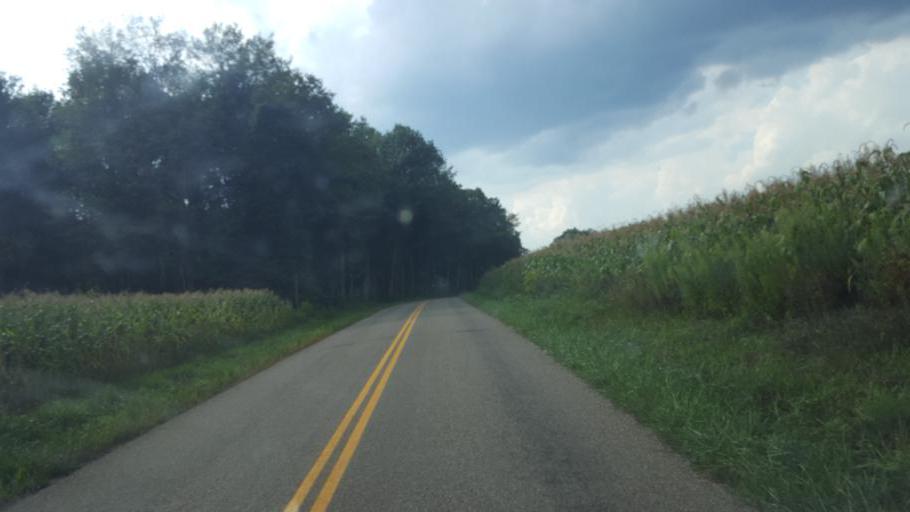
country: US
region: Ohio
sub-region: Knox County
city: Gambier
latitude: 40.3379
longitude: -82.3494
